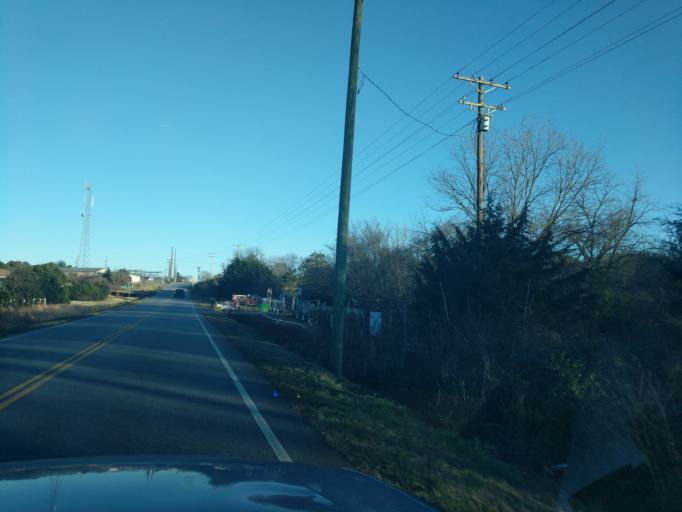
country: US
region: South Carolina
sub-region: Oconee County
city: Westminster
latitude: 34.6008
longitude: -83.0205
